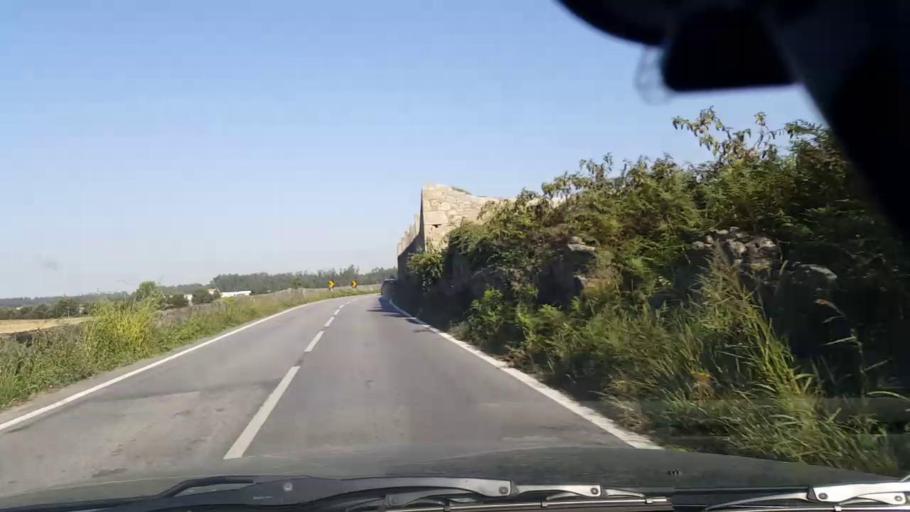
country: PT
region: Porto
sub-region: Vila do Conde
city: Arvore
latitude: 41.3206
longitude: -8.6798
